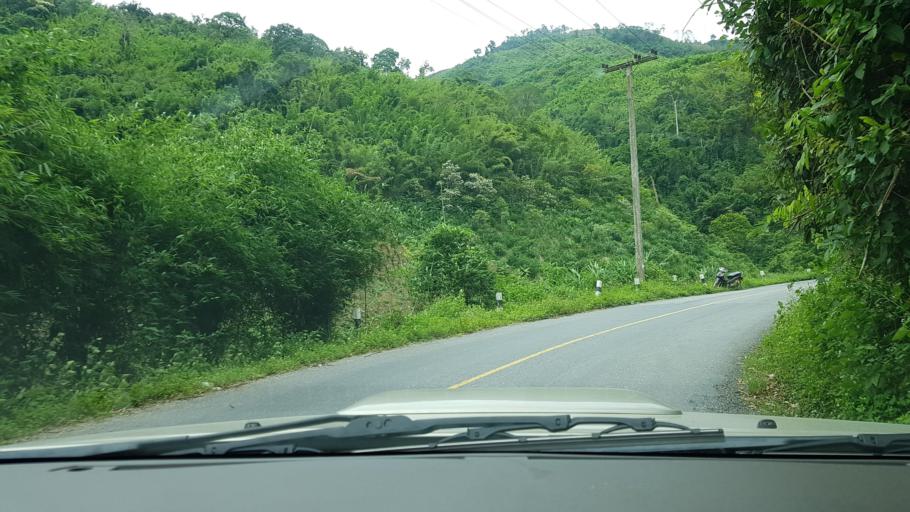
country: LA
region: Oudomxai
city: Muang La
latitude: 20.9197
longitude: 102.2028
